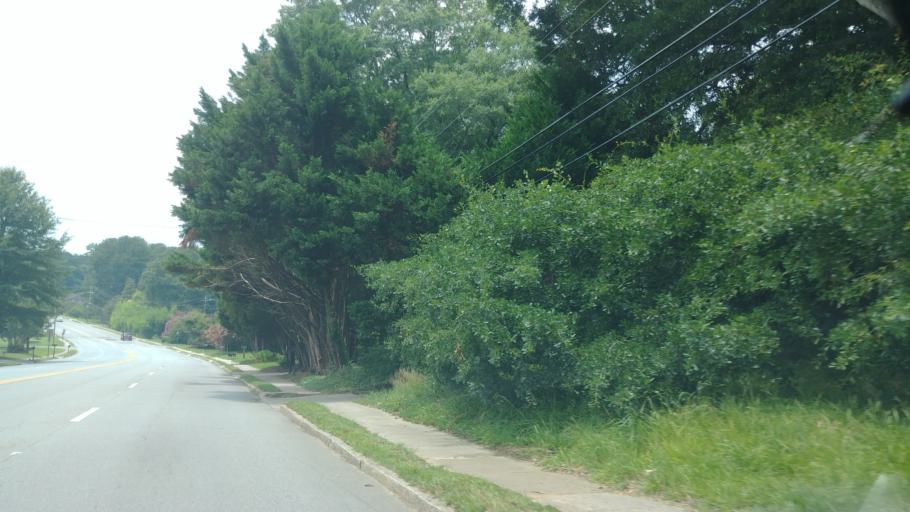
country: US
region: Georgia
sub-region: DeKalb County
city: Chamblee
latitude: 33.8754
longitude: -84.2894
